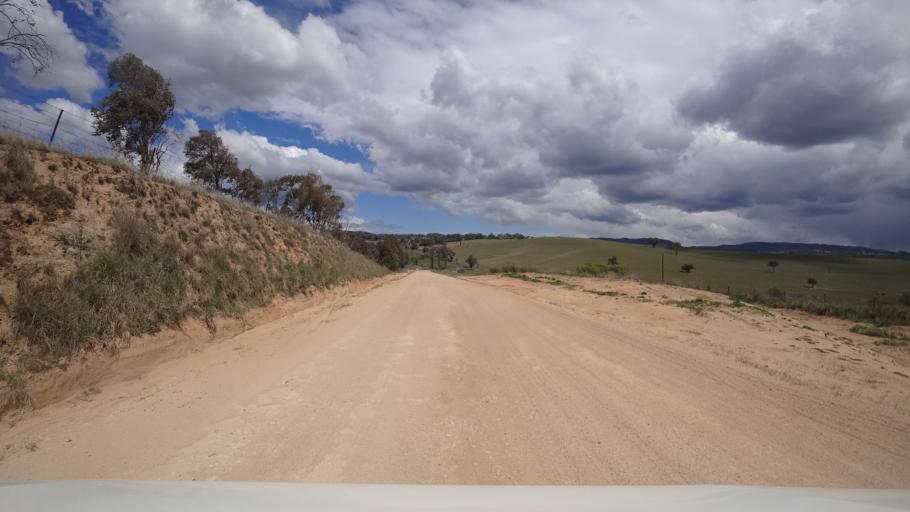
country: AU
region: New South Wales
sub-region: Oberon
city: Oberon
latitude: -33.5770
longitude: 149.8964
